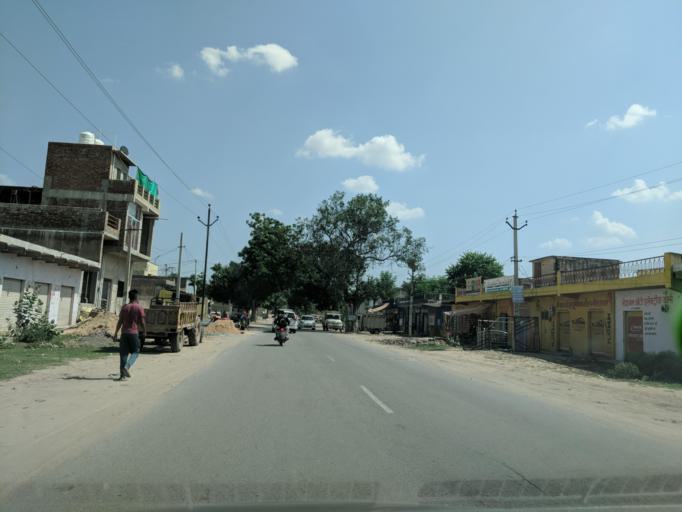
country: IN
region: Rajasthan
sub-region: Jhunjhunun
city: Jhunjhunun
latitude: 28.1368
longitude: 75.3860
